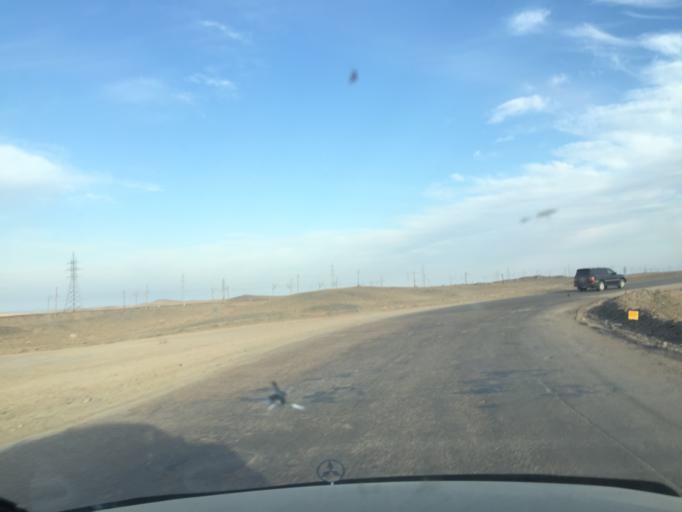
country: KZ
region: Almaty Oblysy
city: Ulken
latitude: 45.2060
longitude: 73.8839
